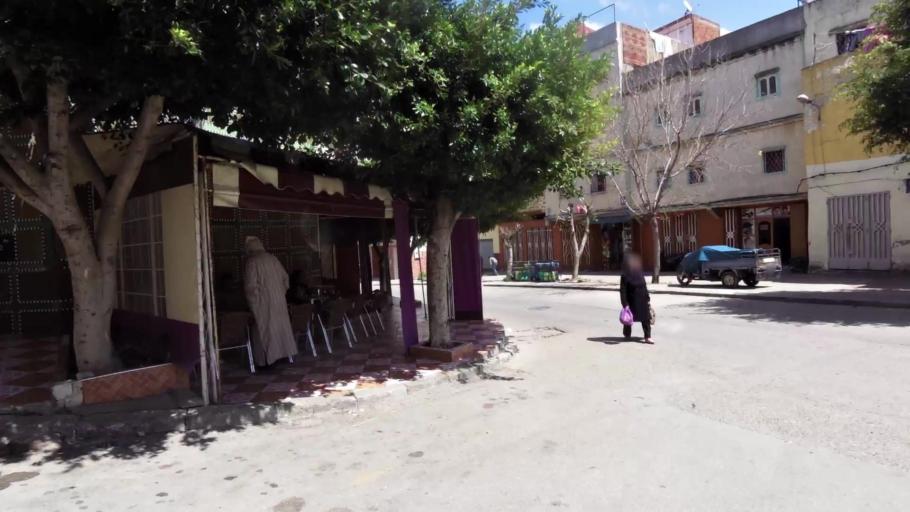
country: MA
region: Tanger-Tetouan
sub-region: Tanger-Assilah
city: Tangier
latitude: 35.7528
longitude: -5.8252
